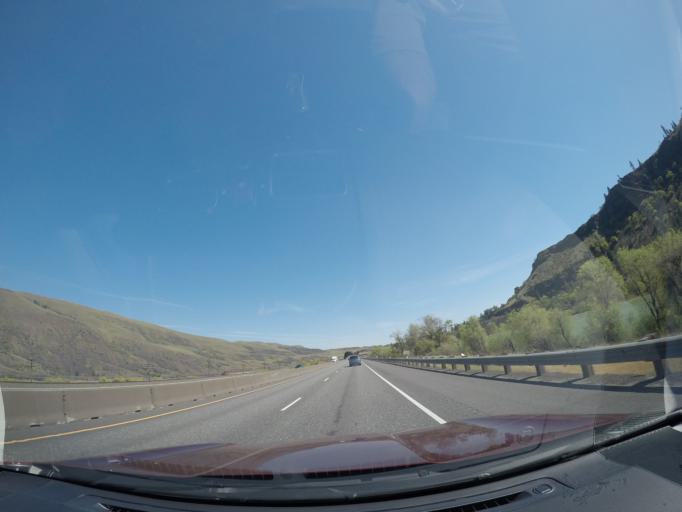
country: US
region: Oregon
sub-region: Wasco County
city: Chenoweth
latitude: 45.6668
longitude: -121.2300
